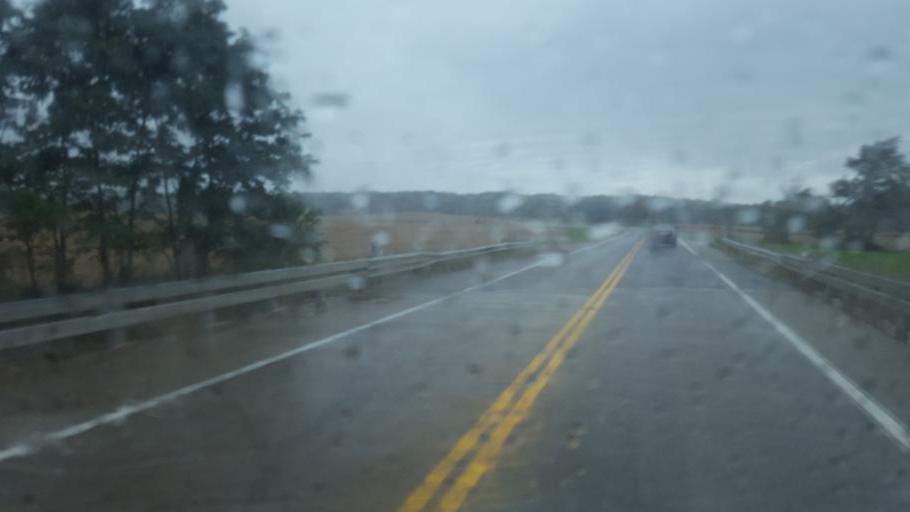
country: US
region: Ohio
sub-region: Richland County
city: Lincoln Heights
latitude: 40.8405
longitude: -82.4742
